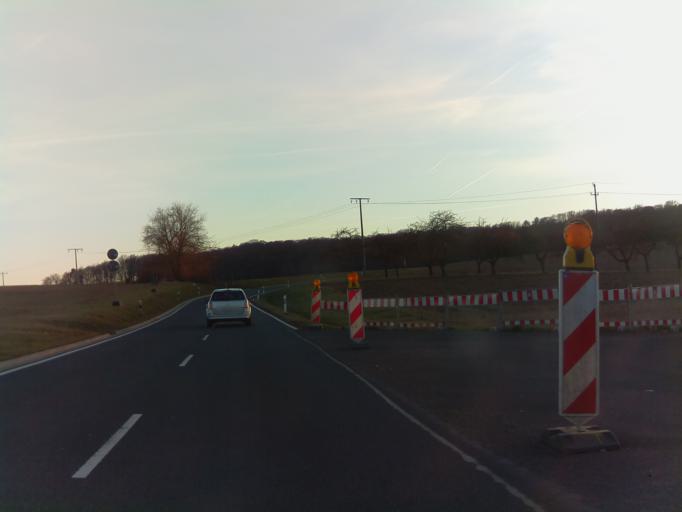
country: DE
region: Bavaria
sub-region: Regierungsbezirk Unterfranken
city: Geiselbach
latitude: 50.1031
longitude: 9.1985
